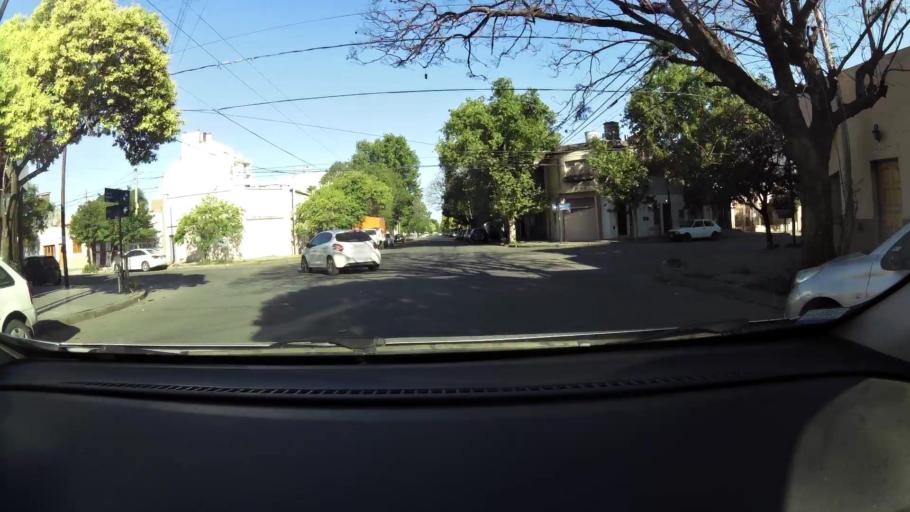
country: AR
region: Cordoba
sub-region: Departamento de Capital
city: Cordoba
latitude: -31.3936
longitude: -64.1808
